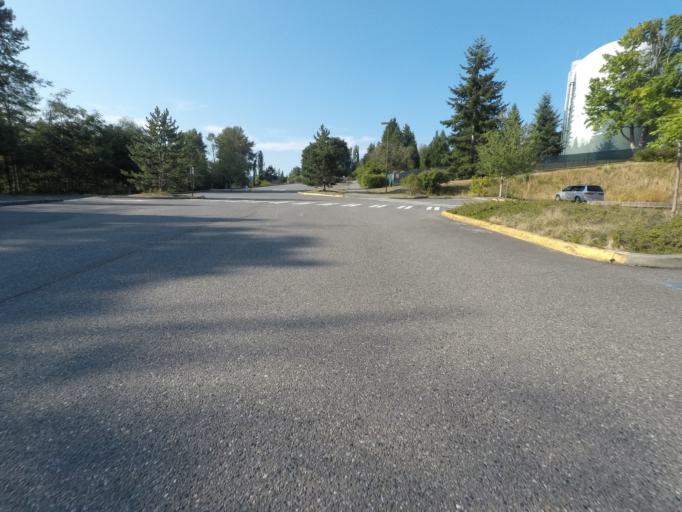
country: US
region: Washington
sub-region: King County
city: Kingsgate
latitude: 47.7421
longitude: -122.1767
